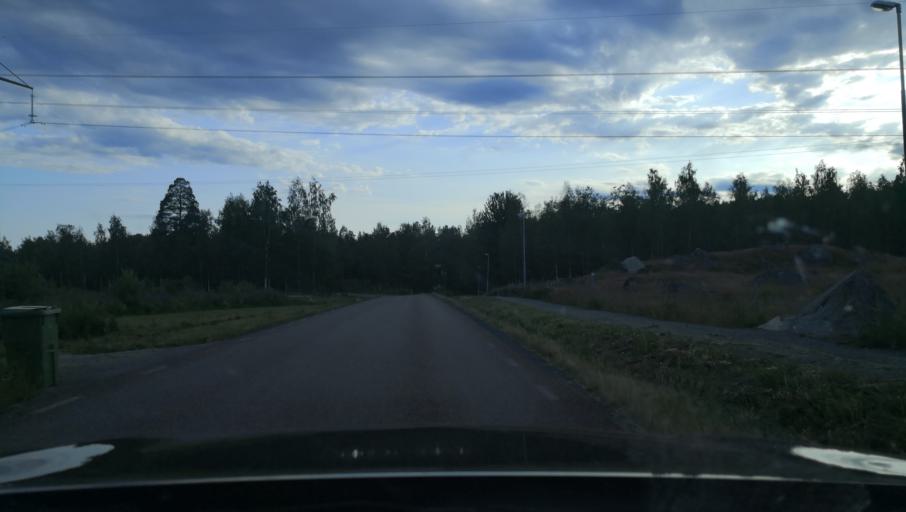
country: SE
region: Dalarna
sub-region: Ludvika Kommun
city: Ludvika
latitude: 60.1204
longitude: 15.2654
